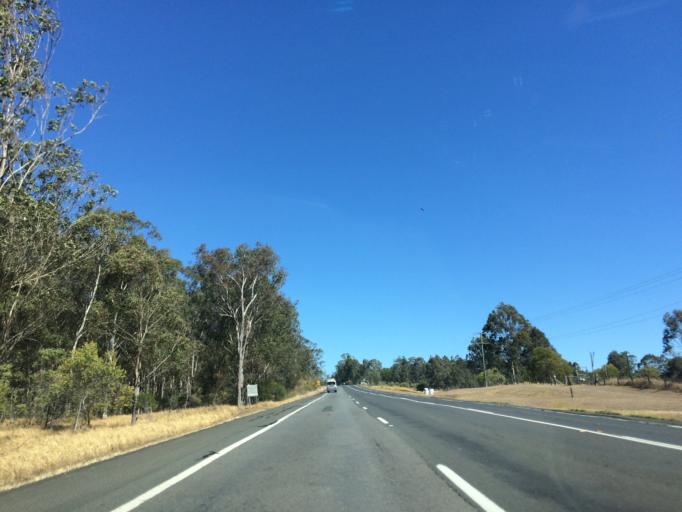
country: AU
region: Queensland
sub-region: Ipswich
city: Thagoona
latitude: -28.0107
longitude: 152.5235
